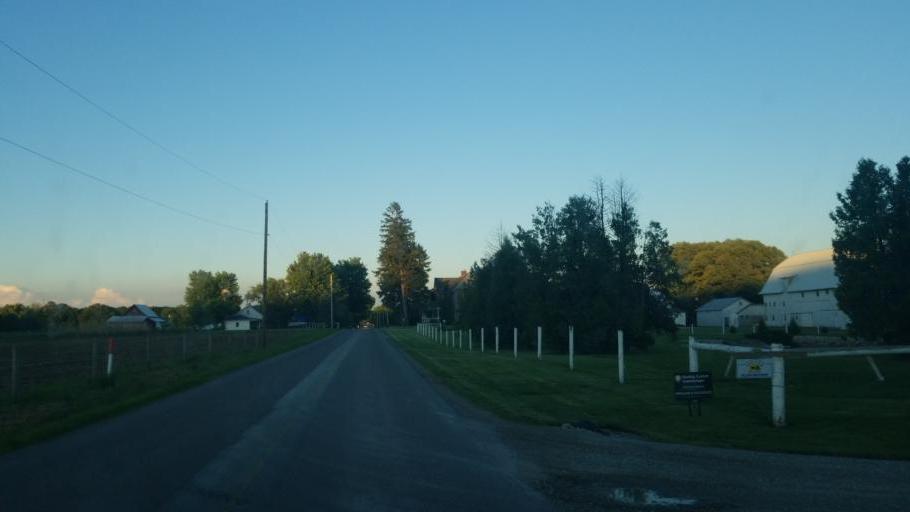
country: US
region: Indiana
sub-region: Elkhart County
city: Nappanee
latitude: 41.4265
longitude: -86.0272
